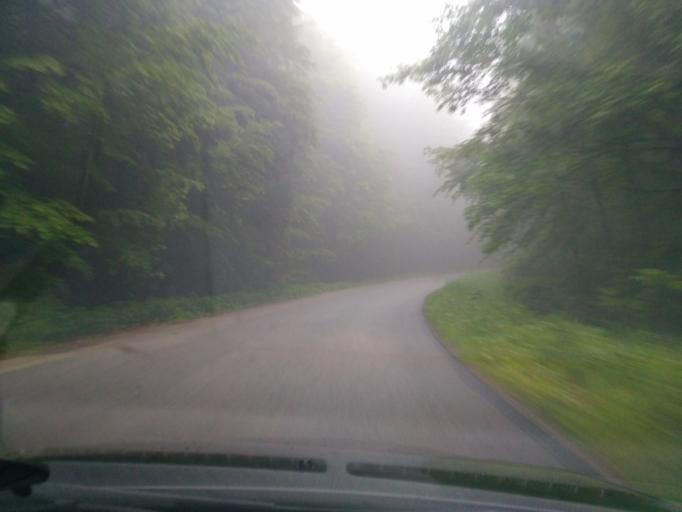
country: PL
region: Subcarpathian Voivodeship
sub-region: Powiat debicki
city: Debica
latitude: 49.9768
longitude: 21.4018
